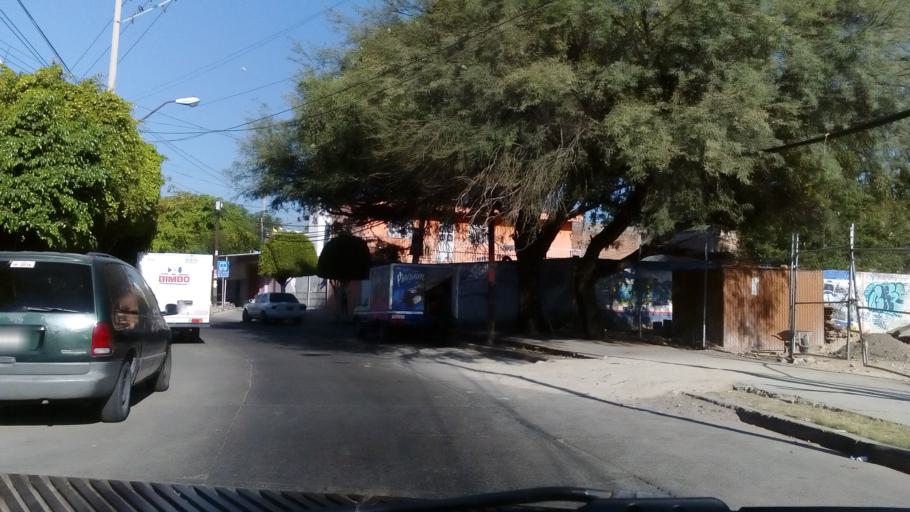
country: MX
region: Guanajuato
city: Leon
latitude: 21.1145
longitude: -101.7009
